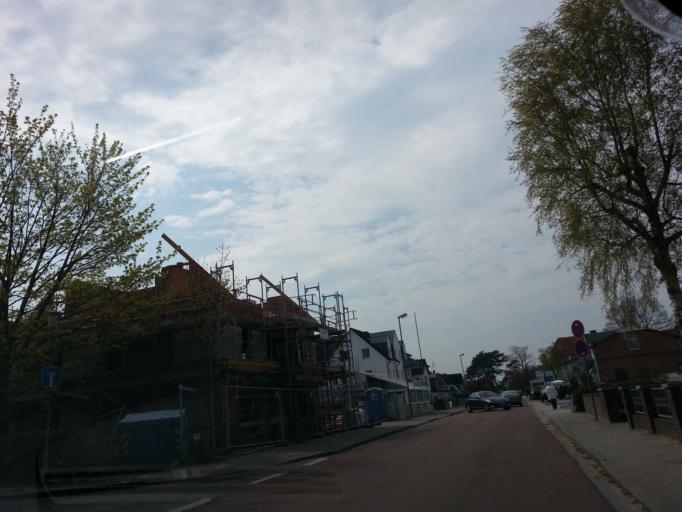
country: DE
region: Schleswig-Holstein
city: Timmendorfer Strand
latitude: 53.9935
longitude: 10.8220
